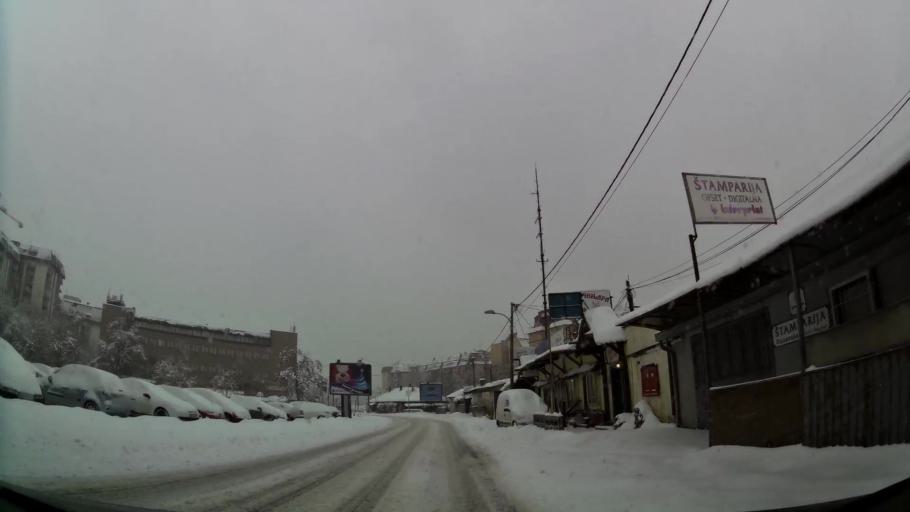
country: RS
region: Central Serbia
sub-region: Belgrade
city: Stari Grad
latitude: 44.8274
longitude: 20.4637
